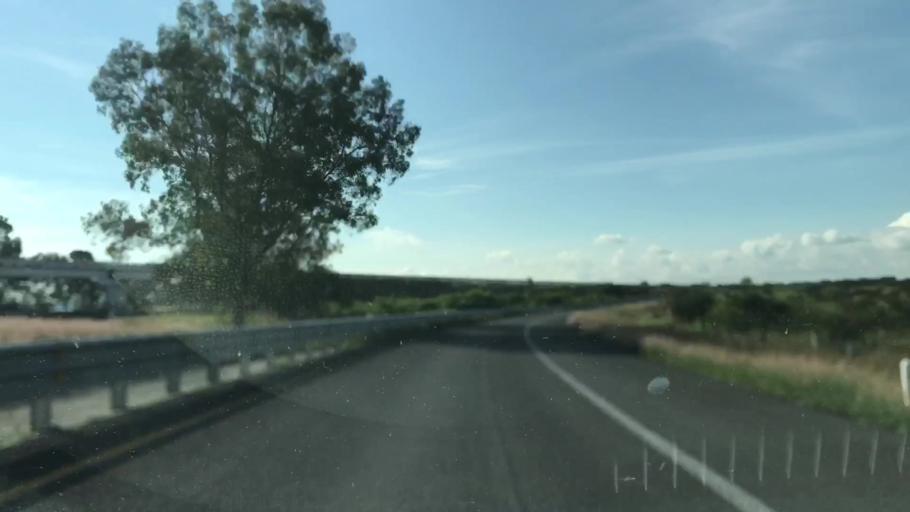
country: MX
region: Jalisco
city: Encarnacion de Diaz
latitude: 21.4496
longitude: -102.2003
